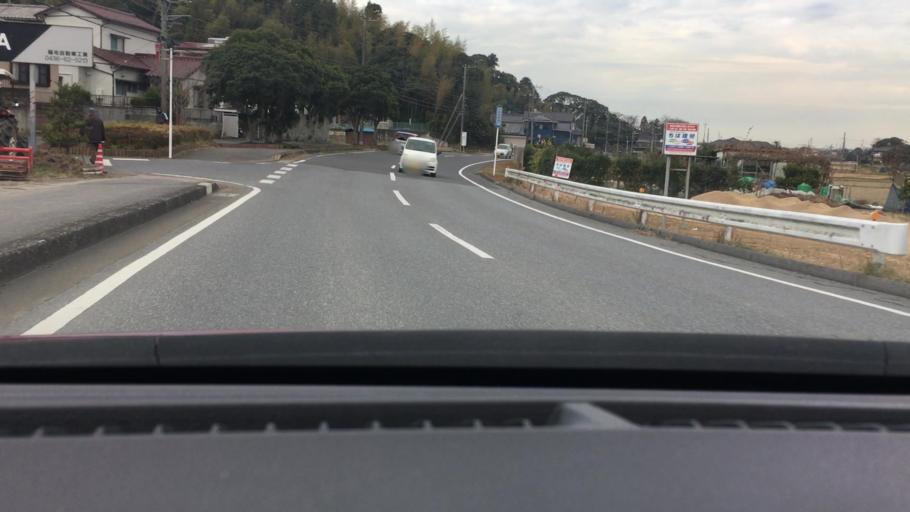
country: JP
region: Chiba
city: Ichihara
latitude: 35.4704
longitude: 140.0642
